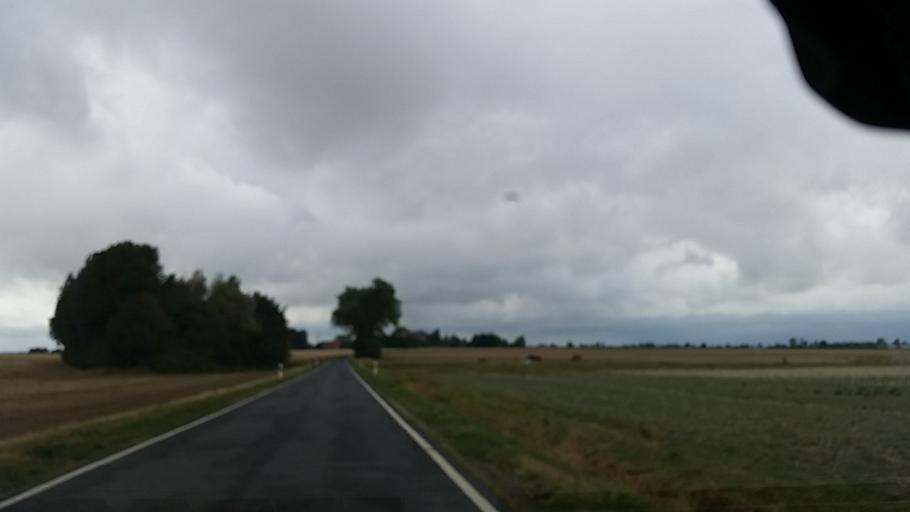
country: DE
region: Lower Saxony
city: Lehre
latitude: 52.3782
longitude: 10.6656
